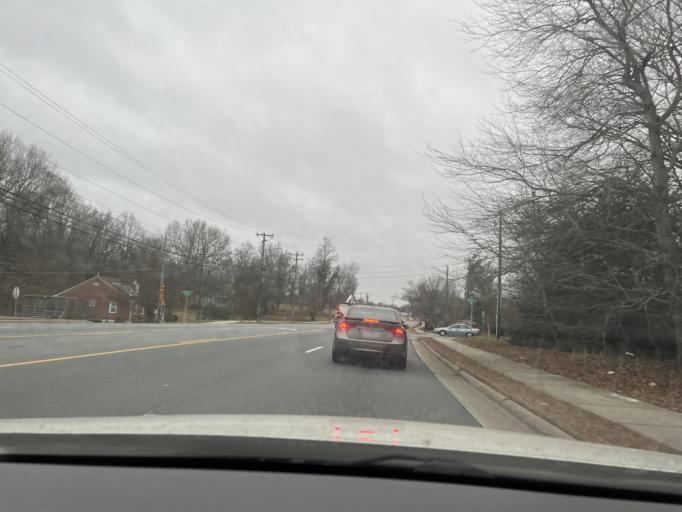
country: US
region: North Carolina
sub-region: Guilford County
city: Greensboro
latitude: 36.0217
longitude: -79.8029
